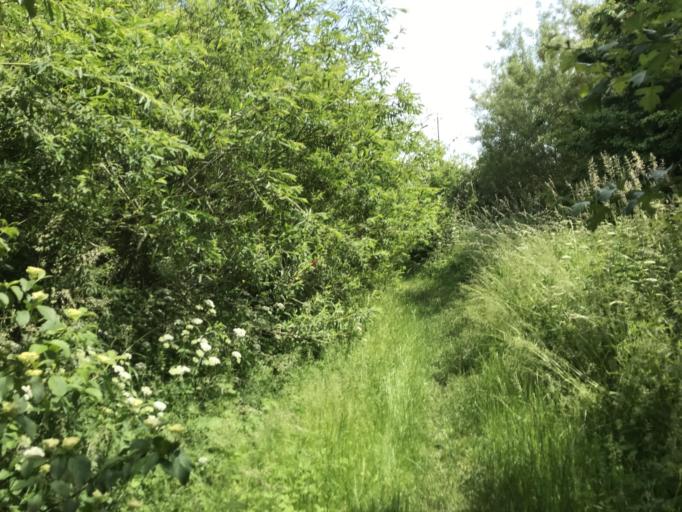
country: SE
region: Skane
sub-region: Landskrona
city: Landskrona
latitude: 55.8955
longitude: 12.8525
